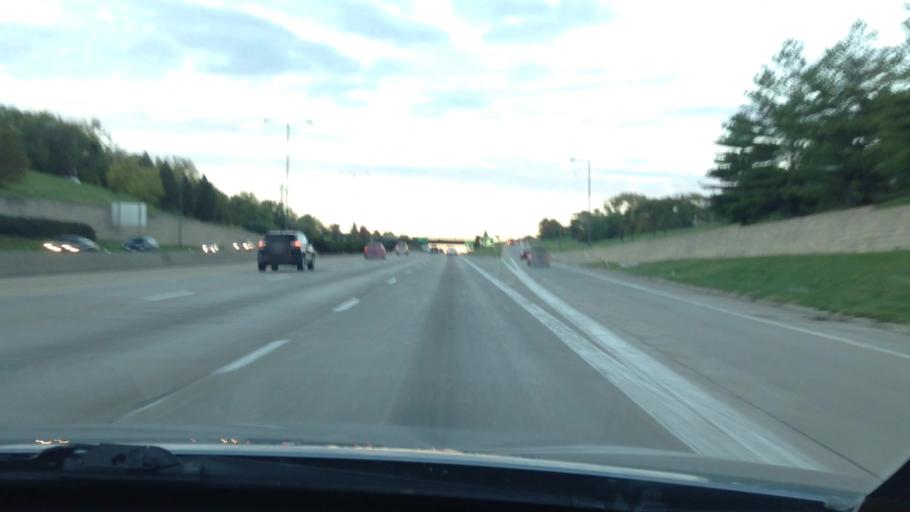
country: US
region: Missouri
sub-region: Jackson County
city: Kansas City
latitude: 39.0505
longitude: -94.5615
